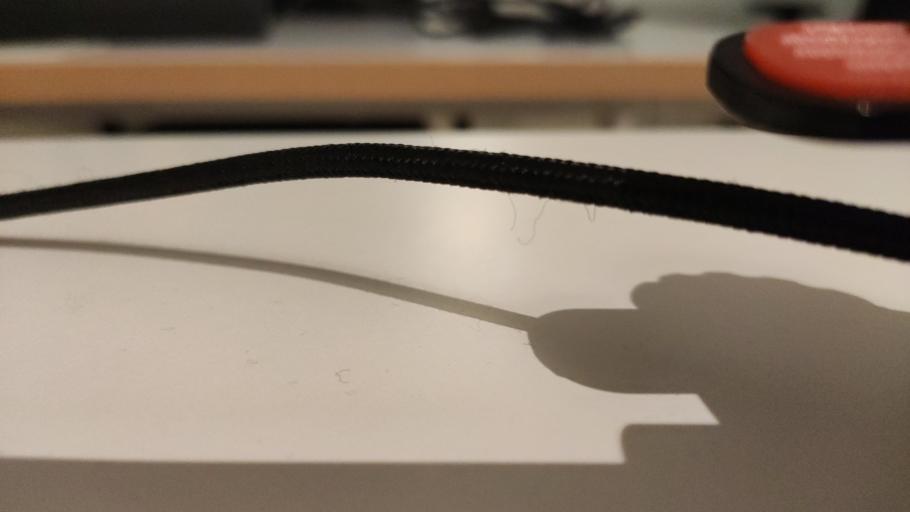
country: RU
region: Moskovskaya
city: Rogachevo
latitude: 56.4050
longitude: 37.2443
